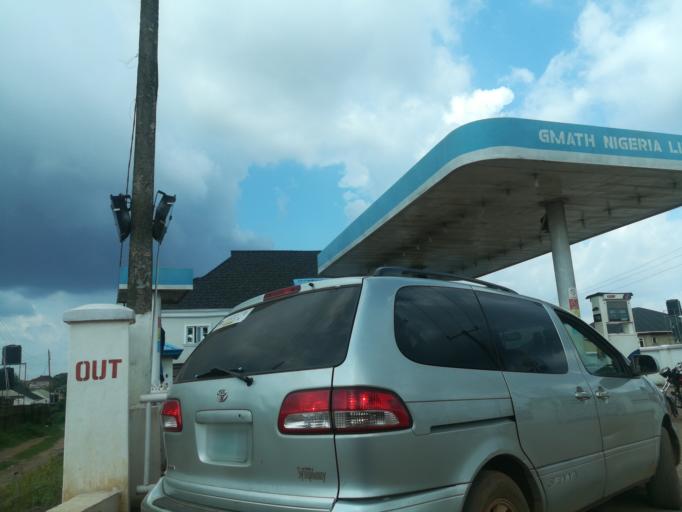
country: NG
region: Oyo
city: Ibadan
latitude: 7.4061
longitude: 3.8304
